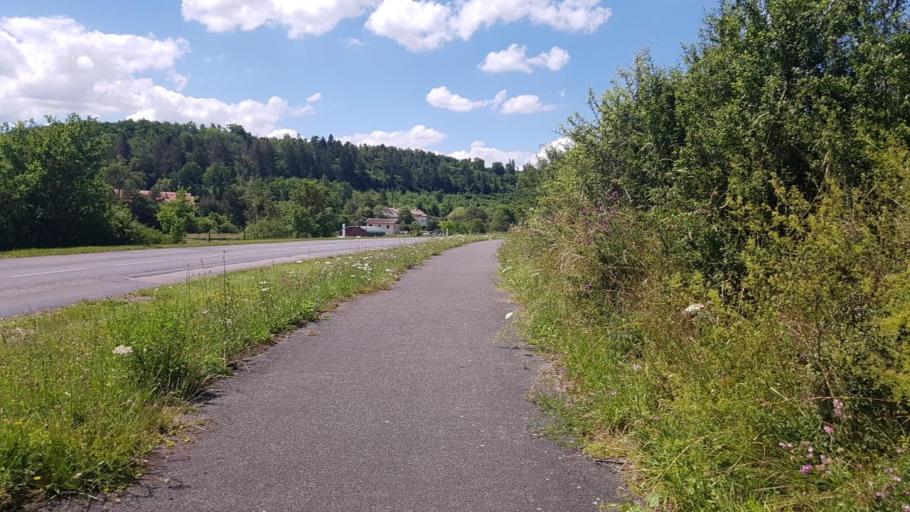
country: FR
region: Lorraine
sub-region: Departement de la Meuse
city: Vacon
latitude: 48.6694
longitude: 5.6082
